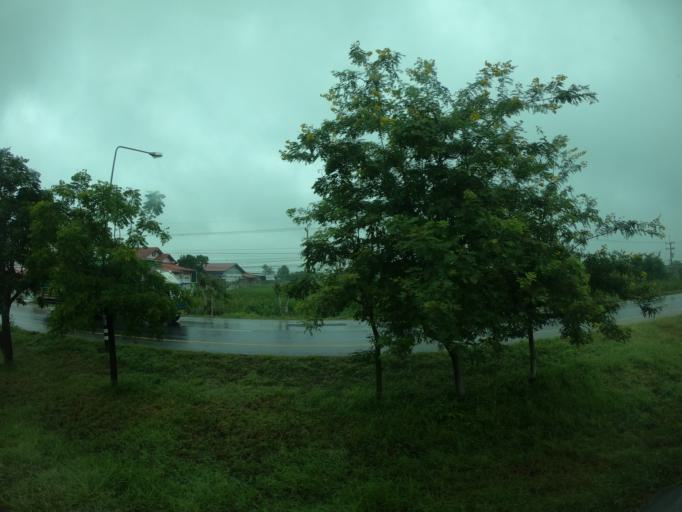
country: TH
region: Nakhon Ratchasima
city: Phimai
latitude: 15.2386
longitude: 102.4237
